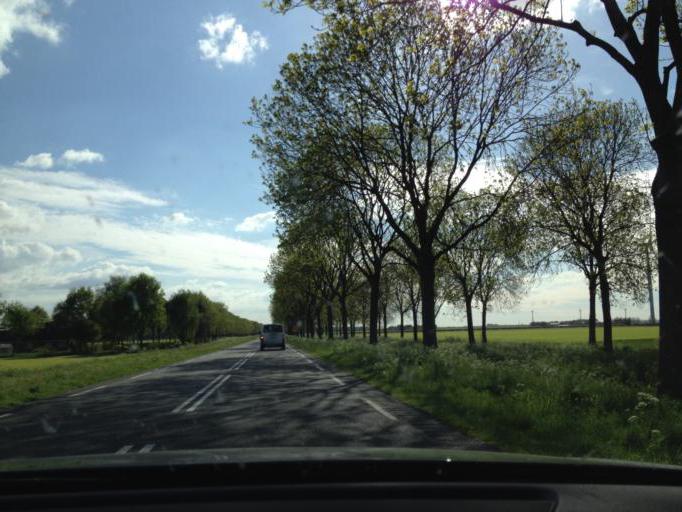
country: NL
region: Utrecht
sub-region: Gemeente Bunschoten
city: Bunschoten
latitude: 52.2766
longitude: 5.4167
